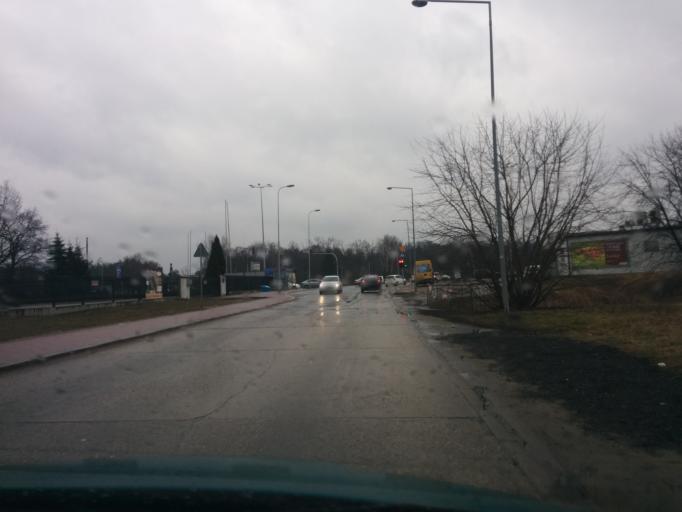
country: PL
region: Masovian Voivodeship
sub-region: Warszawa
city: Bialoleka
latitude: 52.3495
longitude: 20.9449
